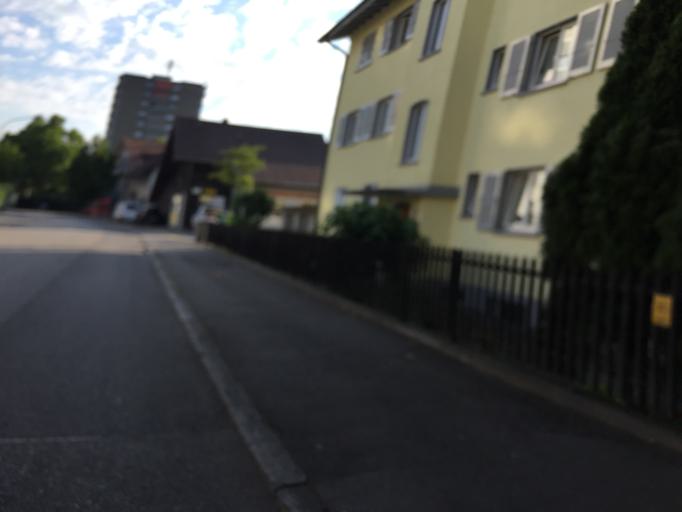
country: CH
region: Bern
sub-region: Bern-Mittelland District
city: Bolligen
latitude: 46.9574
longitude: 7.4908
